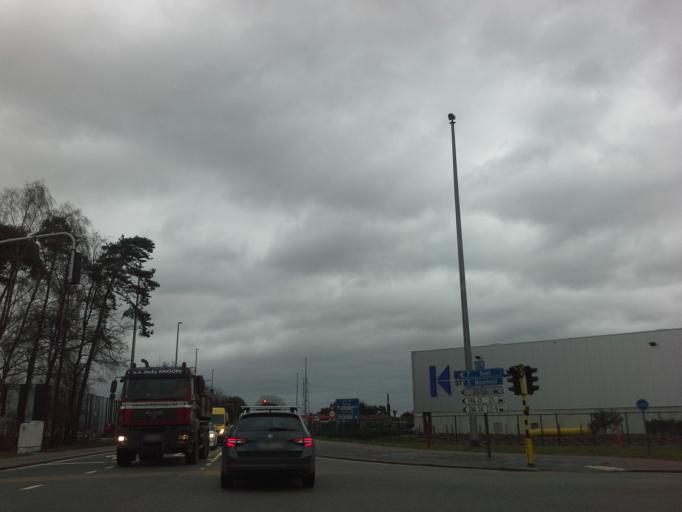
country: BE
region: Flanders
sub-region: Provincie Antwerpen
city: Laakdal
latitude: 51.1094
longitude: 5.0200
